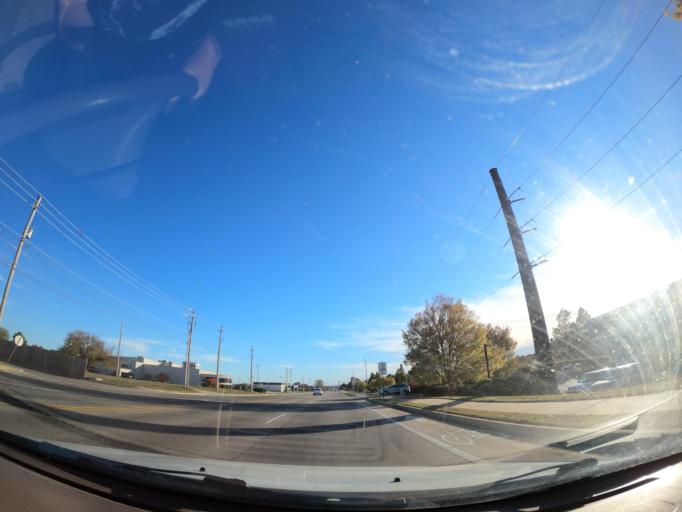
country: US
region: Oklahoma
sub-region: Tulsa County
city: Owasso
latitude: 36.2924
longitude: -95.8303
